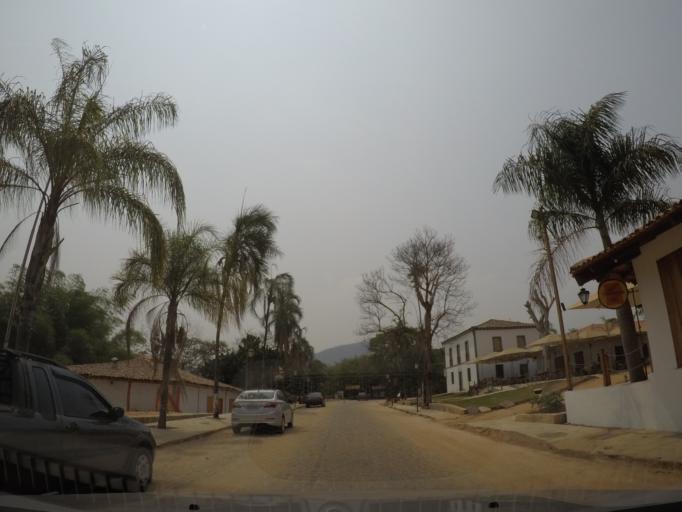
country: BR
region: Goias
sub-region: Pirenopolis
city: Pirenopolis
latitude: -15.8504
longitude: -48.9585
